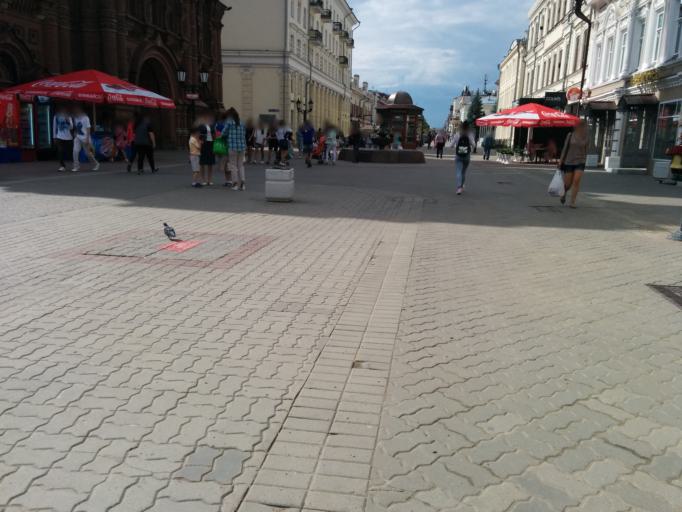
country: RU
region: Tatarstan
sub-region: Gorod Kazan'
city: Kazan
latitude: 55.7882
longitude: 49.1199
